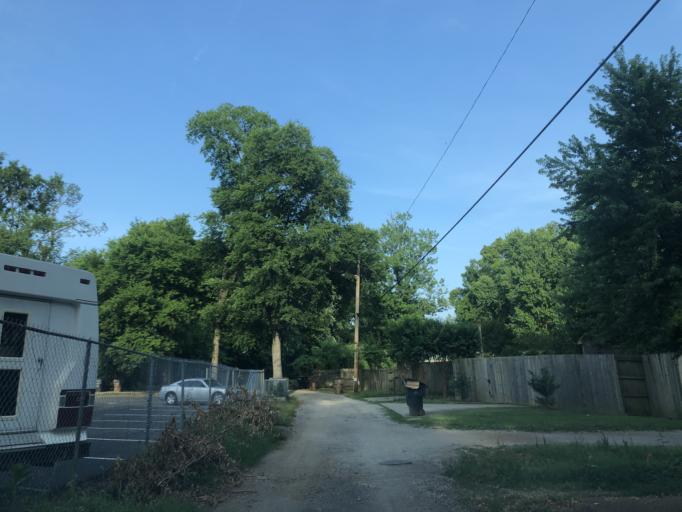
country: US
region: Tennessee
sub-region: Davidson County
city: Nashville
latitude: 36.1310
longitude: -86.7834
